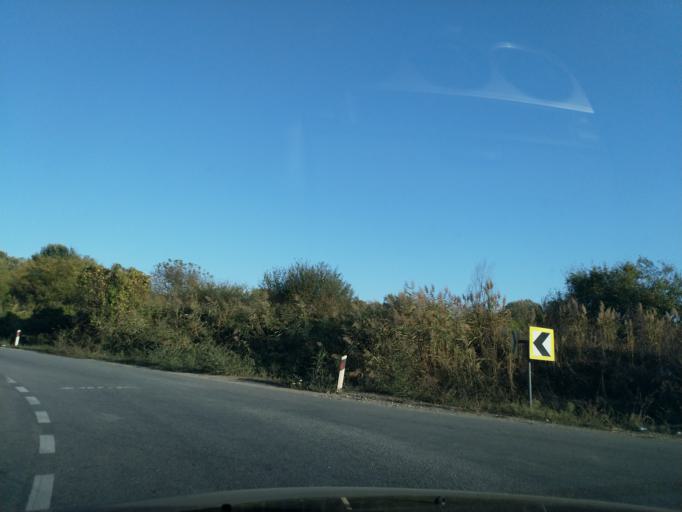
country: RS
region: Central Serbia
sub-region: Pomoravski Okrug
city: Svilajnac
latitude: 44.2233
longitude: 21.1494
